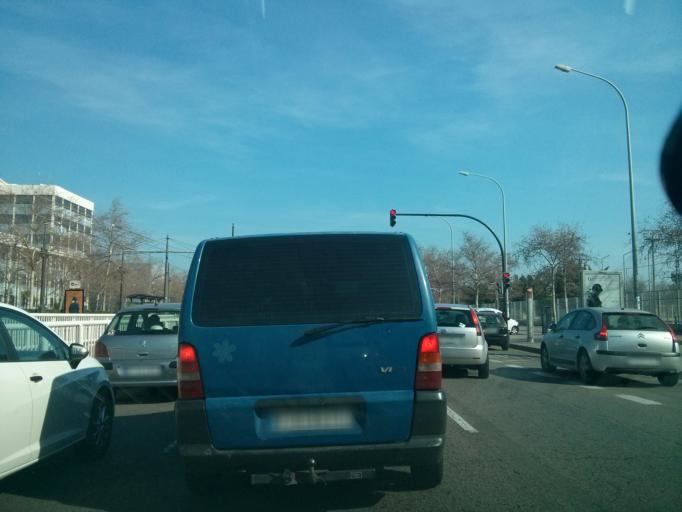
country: ES
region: Valencia
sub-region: Provincia de Valencia
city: Alboraya
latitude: 39.4783
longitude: -0.3403
